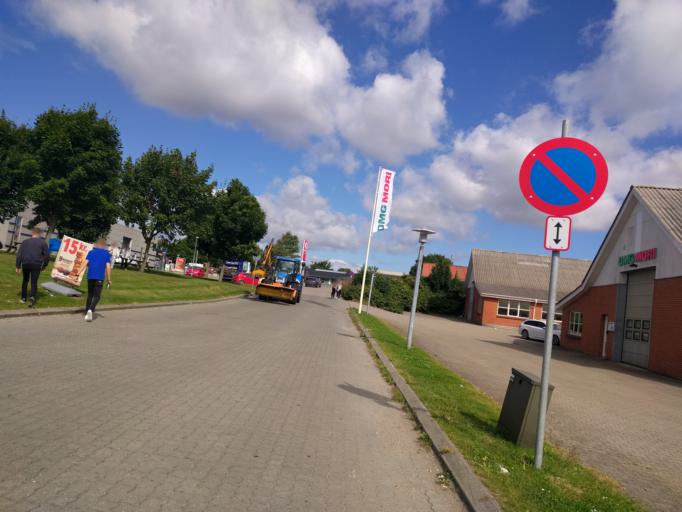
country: DK
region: South Denmark
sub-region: Fredericia Kommune
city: Snoghoj
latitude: 55.5365
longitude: 9.7181
